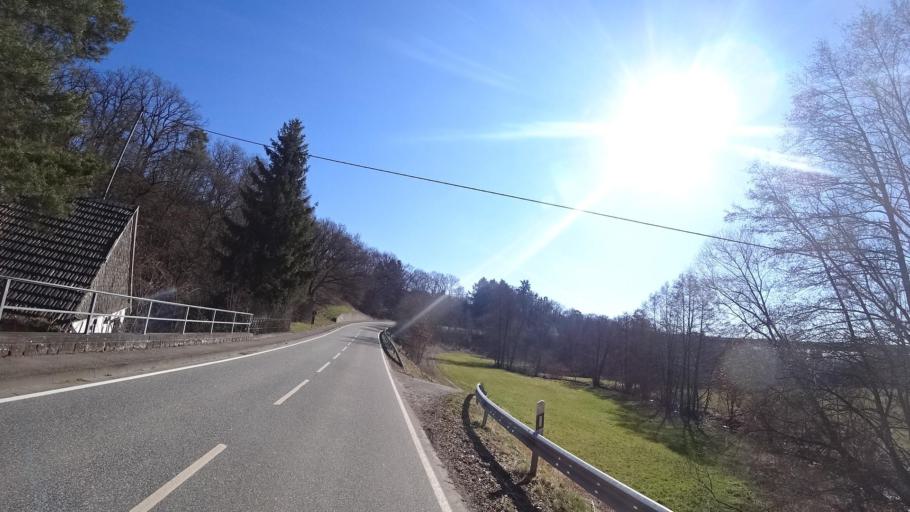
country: DE
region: Rheinland-Pfalz
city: Unzenberg
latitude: 49.9615
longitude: 7.4549
